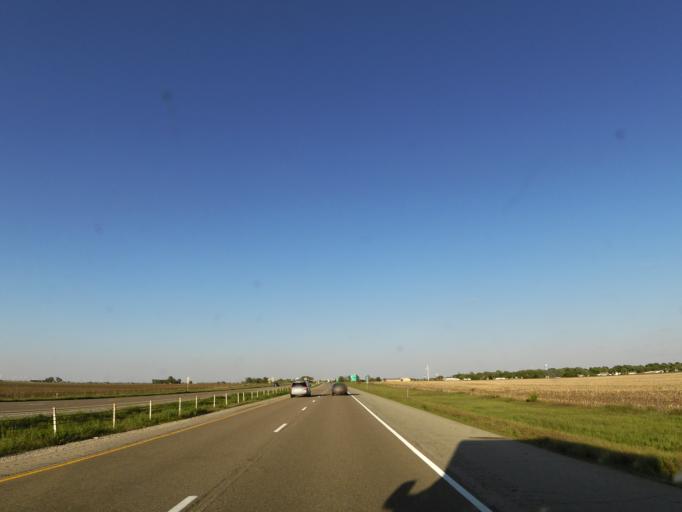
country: US
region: Illinois
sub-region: Champaign County
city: Saint Joseph
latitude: 40.1197
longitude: -87.9746
